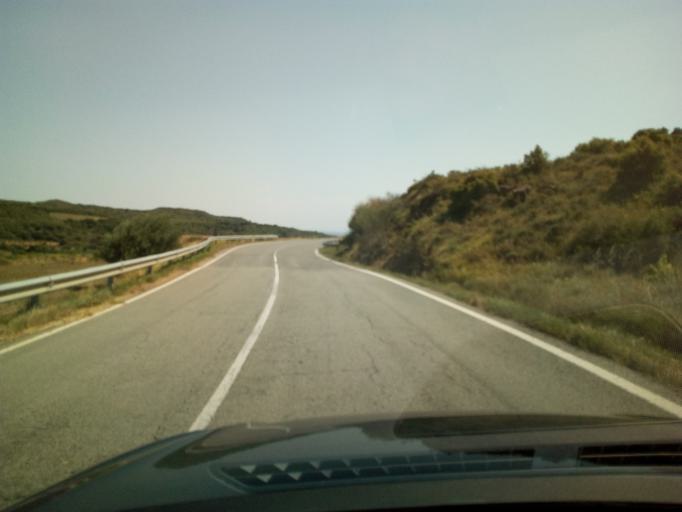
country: ES
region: Navarre
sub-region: Provincia de Navarra
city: San Martin de Unx
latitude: 42.5082
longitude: -1.5678
